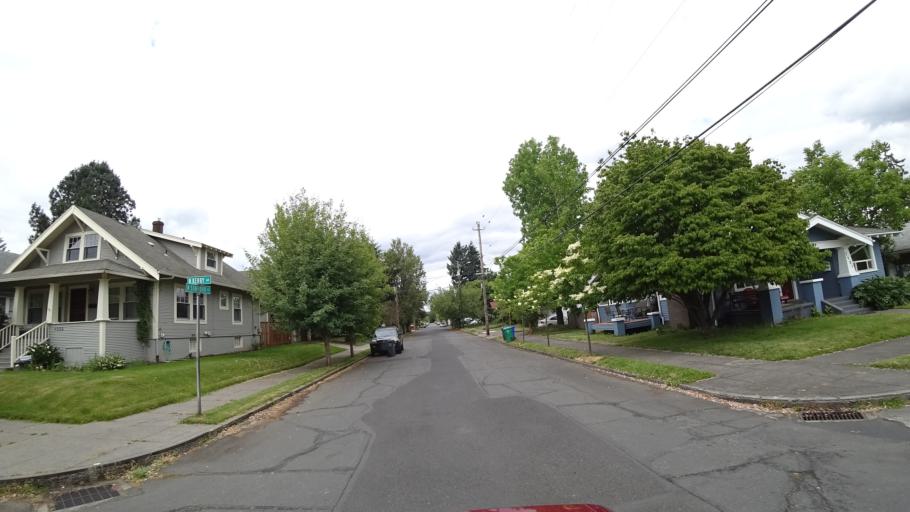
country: US
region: Oregon
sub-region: Multnomah County
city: Portland
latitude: 45.5765
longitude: -122.6729
